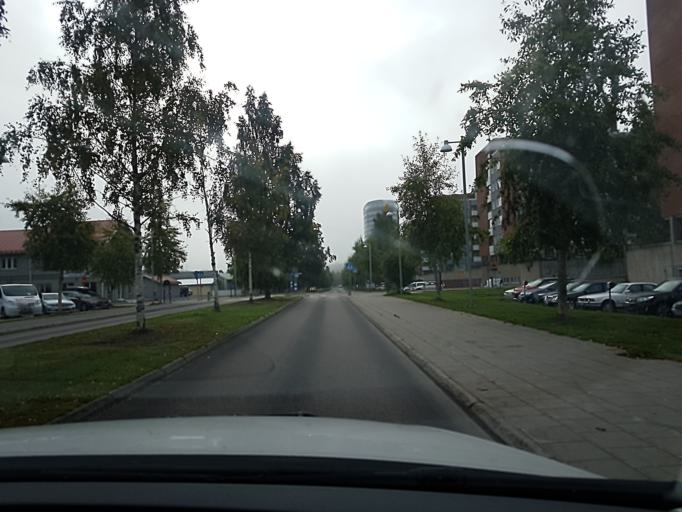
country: SE
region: Norrbotten
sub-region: Pitea Kommun
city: Pitea
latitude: 65.3173
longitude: 21.4842
